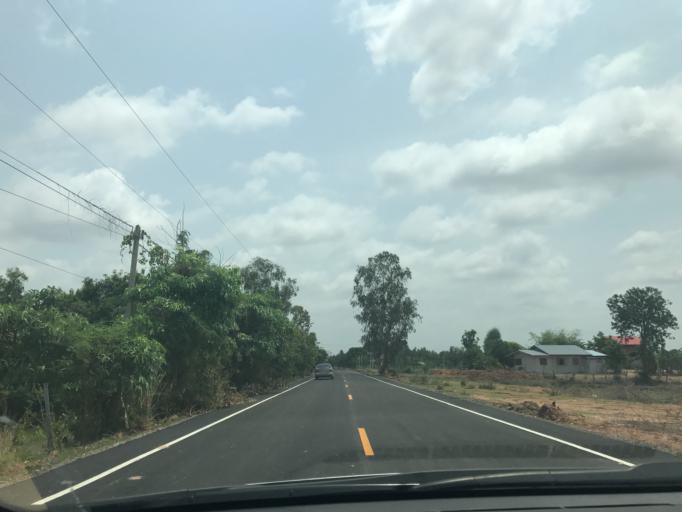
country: TH
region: Surin
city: Khwao Sinarin
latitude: 15.0424
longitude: 103.6501
